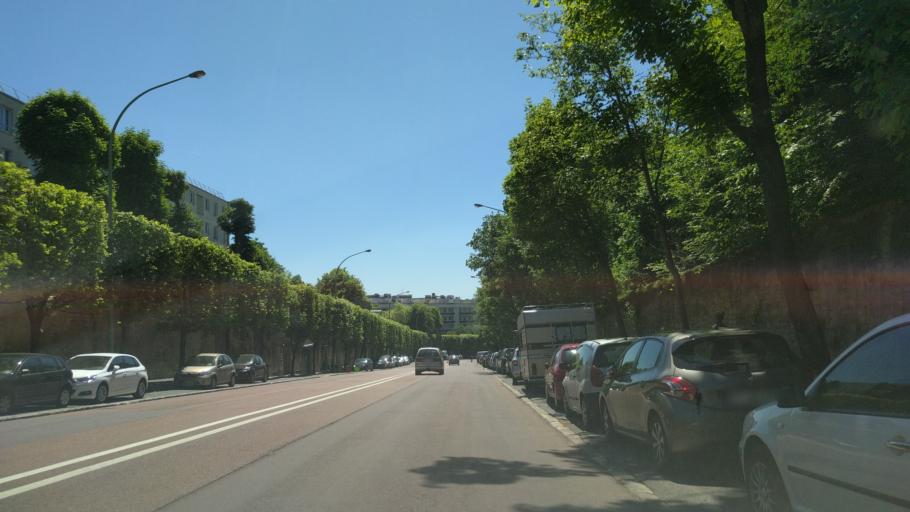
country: FR
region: Ile-de-France
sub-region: Departement des Yvelines
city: Le Pecq
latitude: 48.8924
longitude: 2.0996
